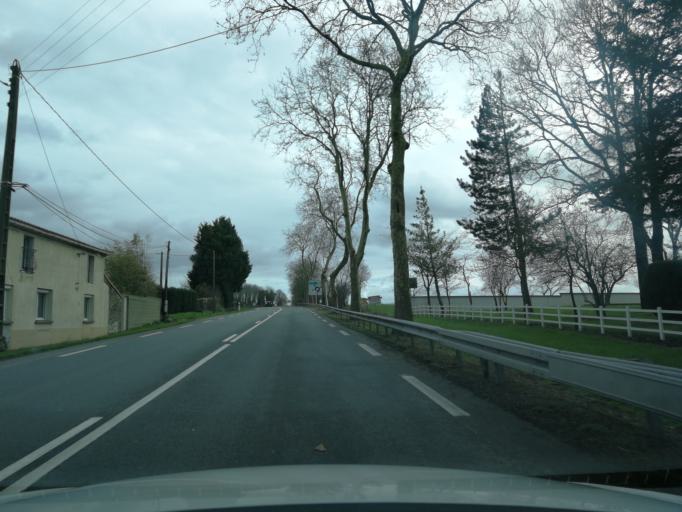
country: FR
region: Pays de la Loire
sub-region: Departement de la Vendee
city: Saint-Fulgent
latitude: 46.8658
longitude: -1.1921
